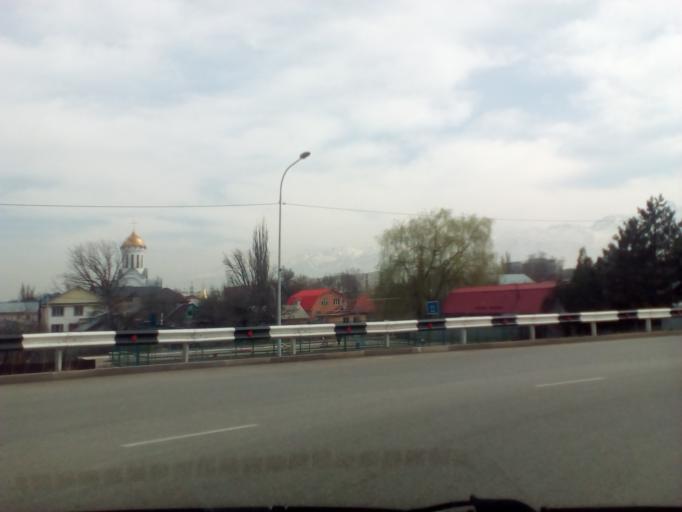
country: KZ
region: Almaty Qalasy
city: Almaty
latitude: 43.2454
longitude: 76.8276
